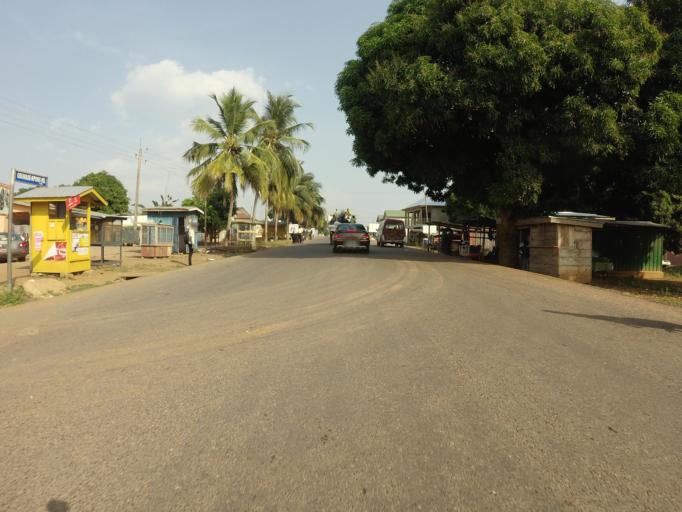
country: GH
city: Akropong
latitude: 6.1579
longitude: 0.0523
